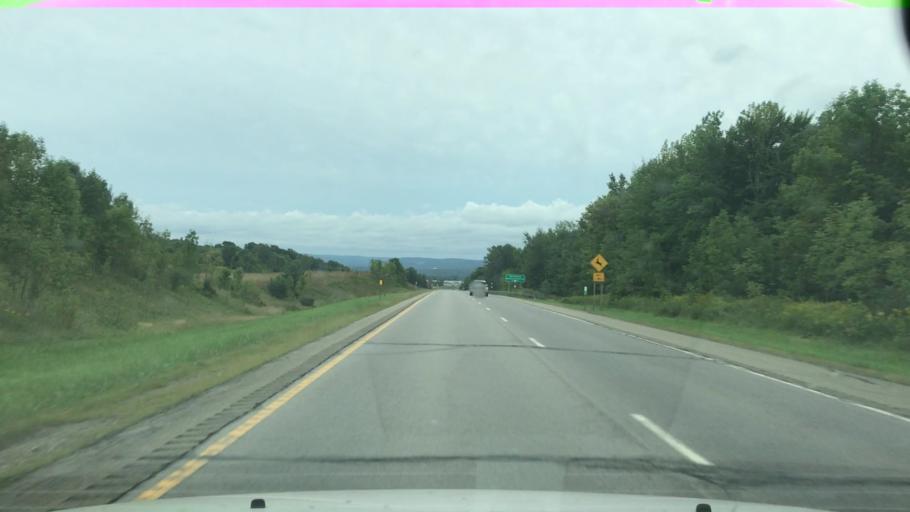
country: US
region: New York
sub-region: Erie County
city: Springville
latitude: 42.5266
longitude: -78.7013
